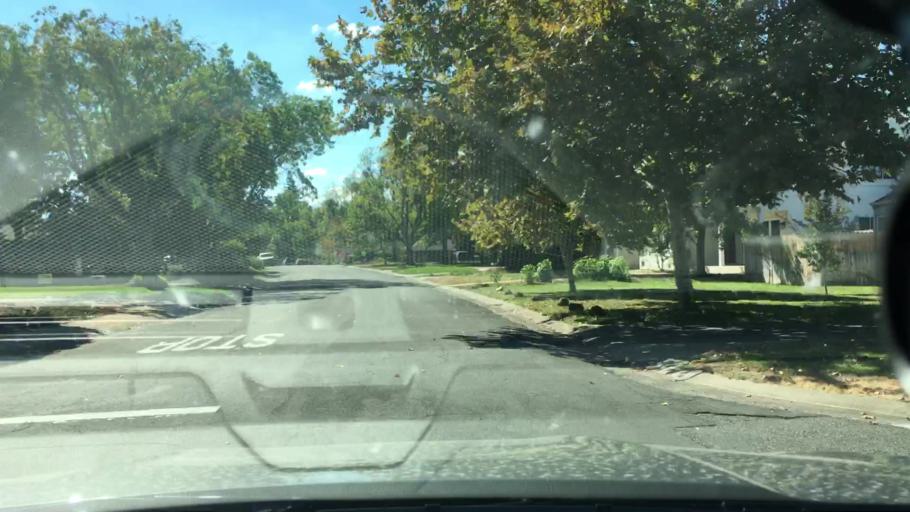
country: US
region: California
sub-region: Sacramento County
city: Arden-Arcade
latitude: 38.5828
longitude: -121.3789
